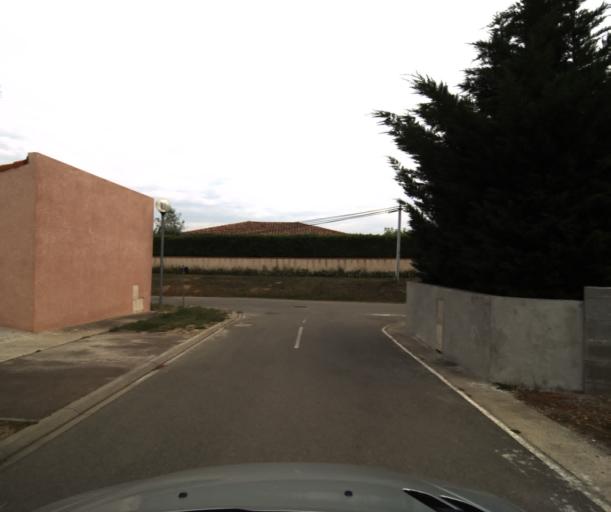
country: FR
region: Midi-Pyrenees
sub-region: Departement de la Haute-Garonne
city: Lacasse
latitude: 43.4187
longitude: 1.2781
